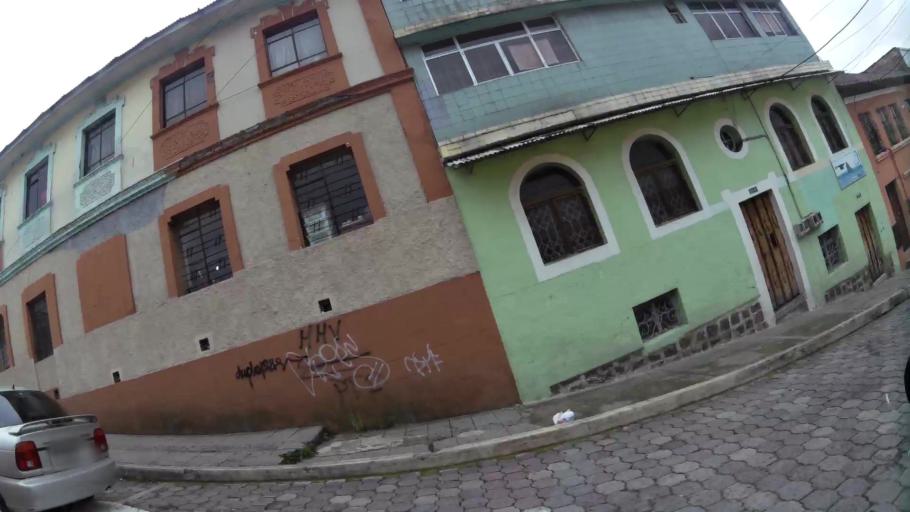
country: EC
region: Pichincha
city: Quito
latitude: -0.2120
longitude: -78.5099
